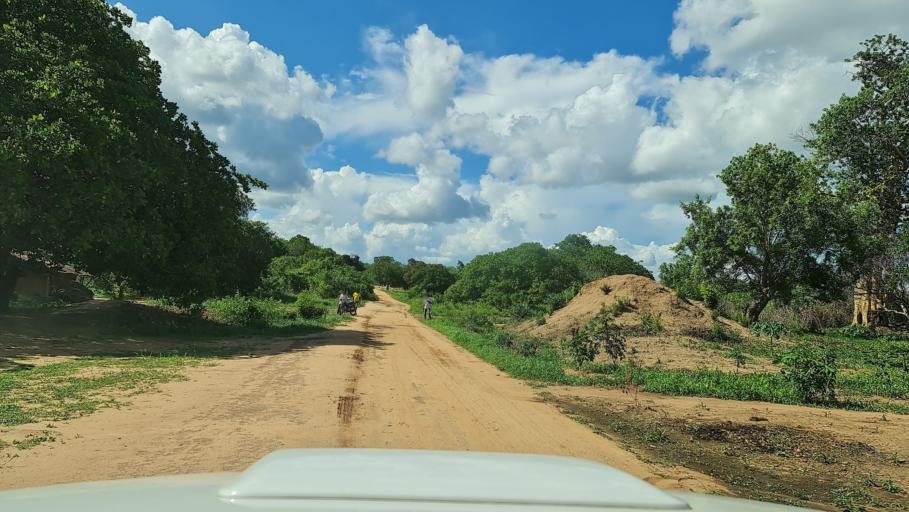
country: MZ
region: Nampula
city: Ilha de Mocambique
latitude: -15.4250
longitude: 40.2692
